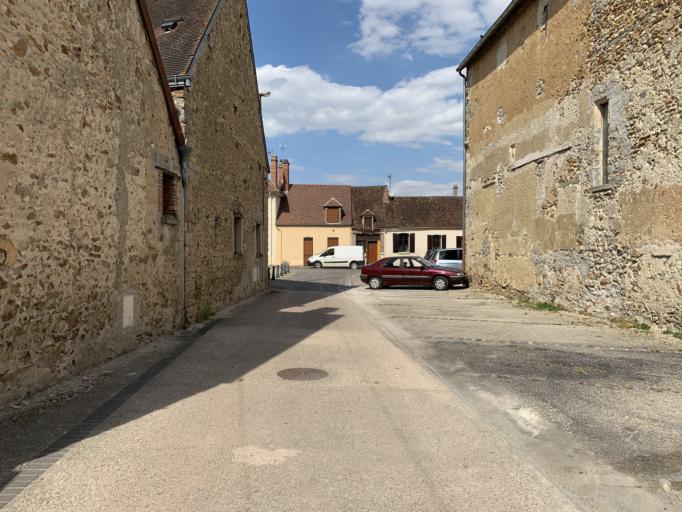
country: FR
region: Champagne-Ardenne
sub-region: Departement de l'Aube
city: Villenauxe-la-Grande
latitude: 48.5903
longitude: 3.5535
